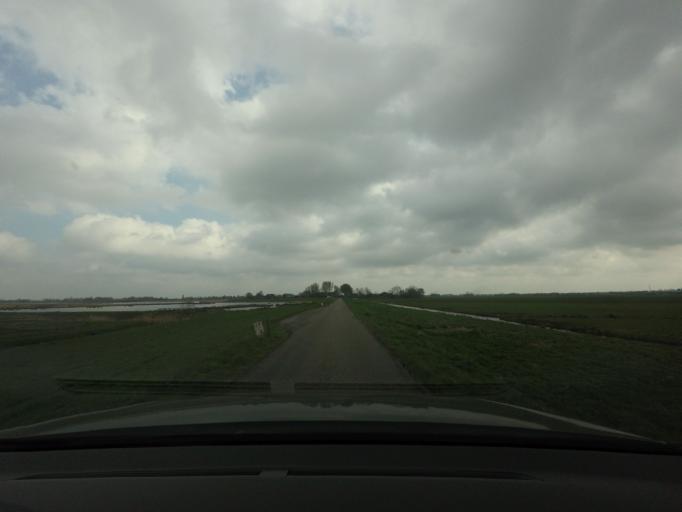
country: NL
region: Utrecht
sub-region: Gemeente De Ronde Venen
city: Mijdrecht
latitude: 52.1724
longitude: 4.8242
